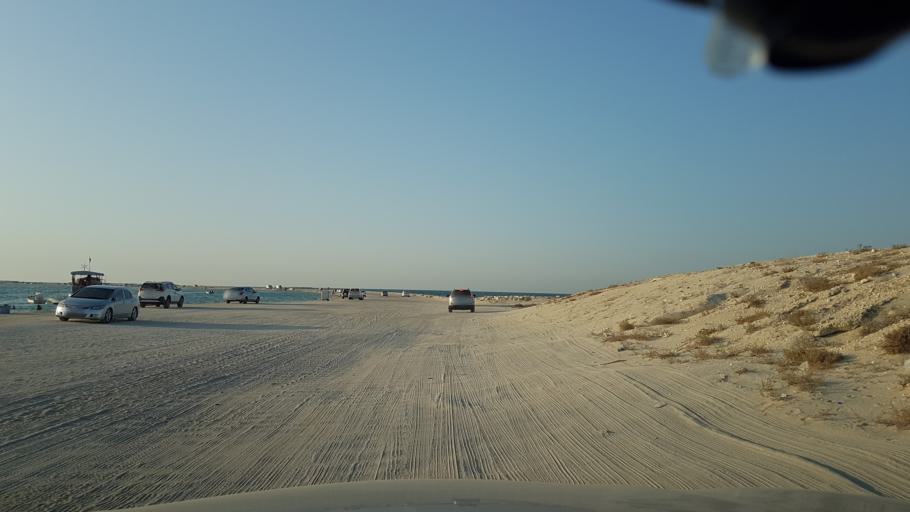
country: BH
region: Manama
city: Jidd Hafs
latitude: 26.2472
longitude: 50.5027
